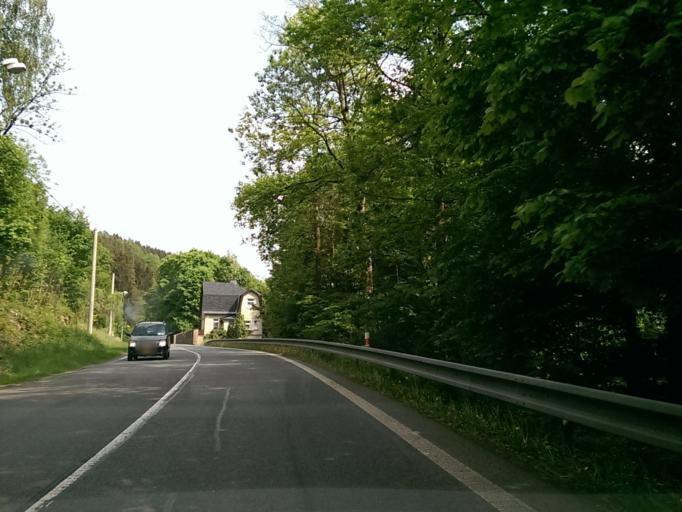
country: CZ
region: Liberecky
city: Zelezny Brod
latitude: 50.6455
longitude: 15.2313
